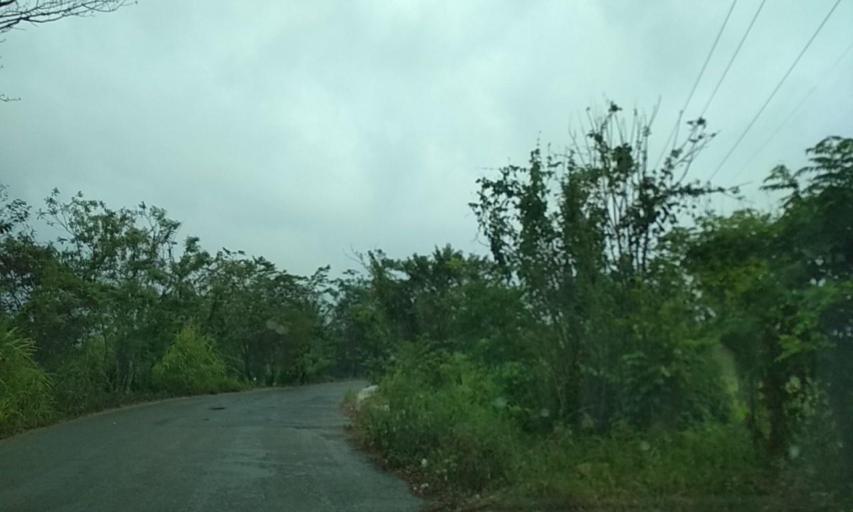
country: MX
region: Tabasco
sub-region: Huimanguillo
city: Francisco Rueda
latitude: 17.5816
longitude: -94.0938
